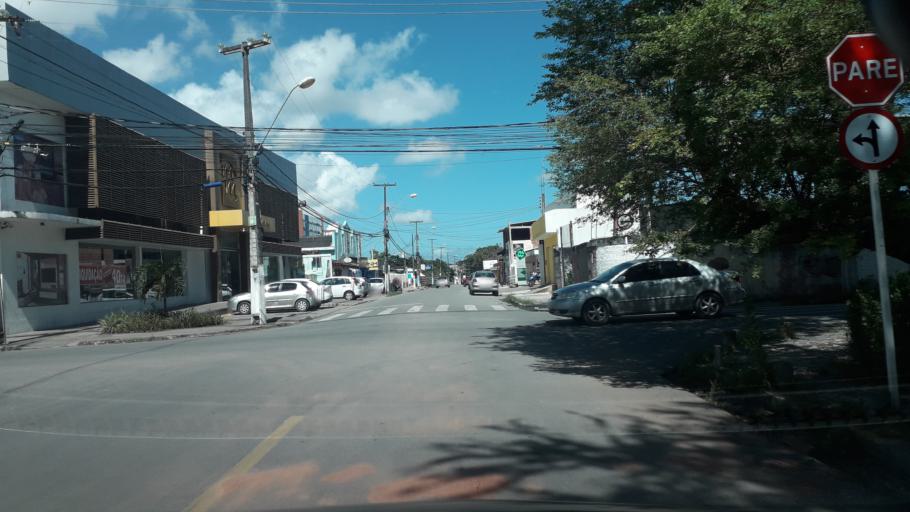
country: BR
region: Alagoas
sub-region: Satuba
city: Satuba
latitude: -9.5781
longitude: -35.7714
